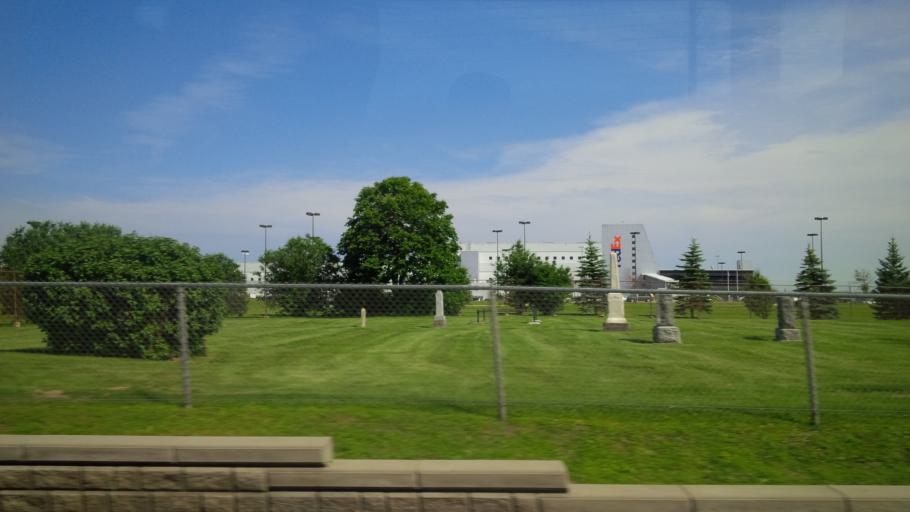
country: CA
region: Ontario
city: Etobicoke
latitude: 43.6858
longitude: -79.6623
